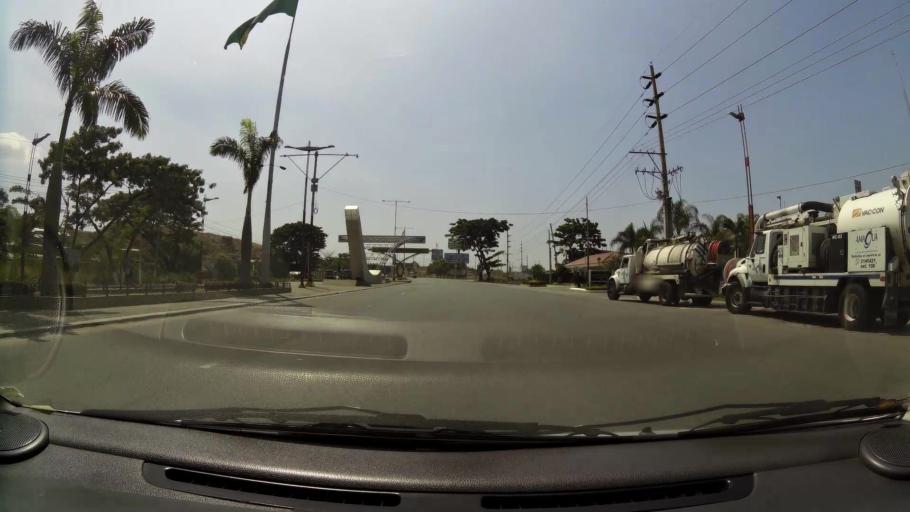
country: EC
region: Guayas
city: Eloy Alfaro
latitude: -2.0626
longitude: -79.8722
